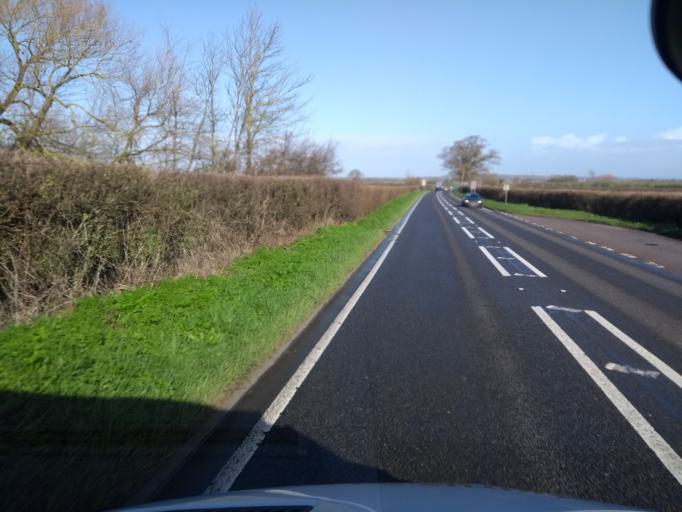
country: GB
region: England
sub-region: Somerset
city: Ilchester
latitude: 50.9774
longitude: -2.6729
